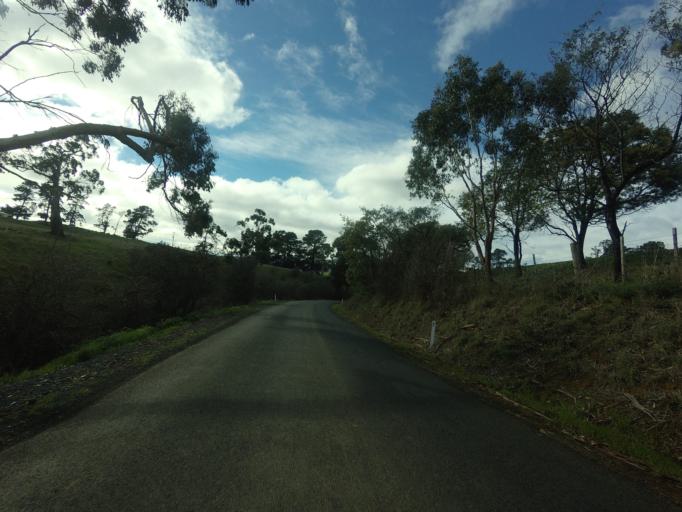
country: AU
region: Tasmania
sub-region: Derwent Valley
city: New Norfolk
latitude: -42.7111
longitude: 146.8948
